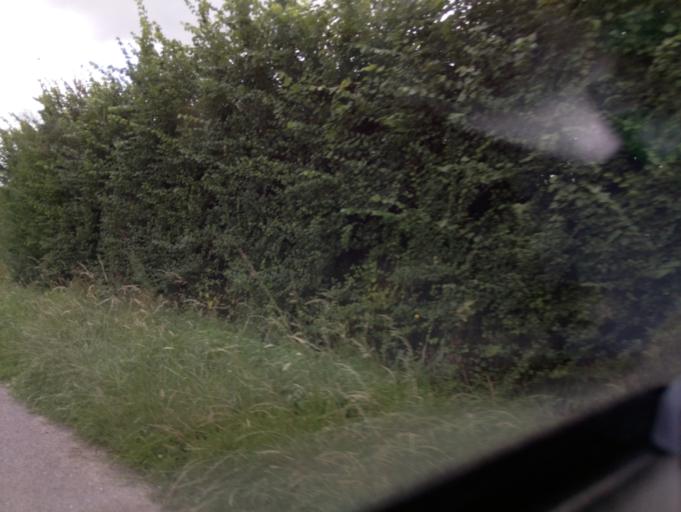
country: GB
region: England
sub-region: Oxfordshire
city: Faringdon
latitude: 51.6171
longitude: -1.6029
